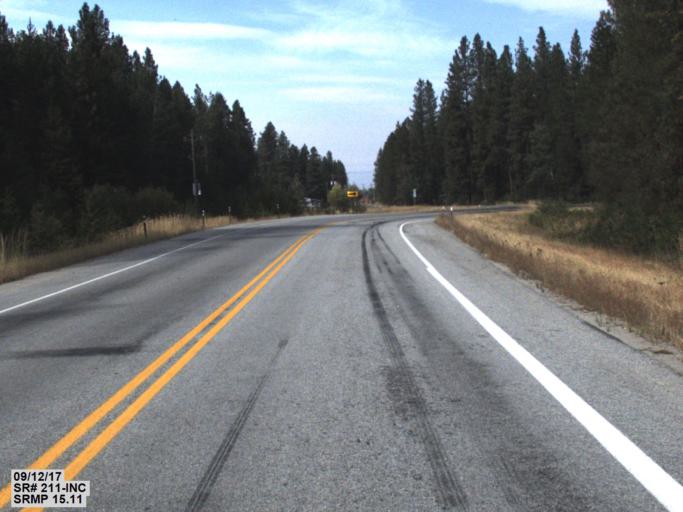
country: US
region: Washington
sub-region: Pend Oreille County
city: Newport
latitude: 48.3041
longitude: -117.2844
